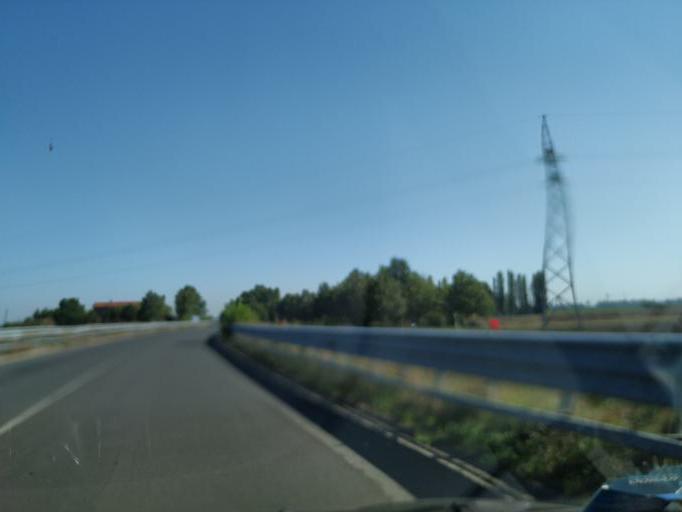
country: IT
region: Emilia-Romagna
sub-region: Provincia di Bologna
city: San Giovanni in Persiceto
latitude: 44.6730
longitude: 11.1914
